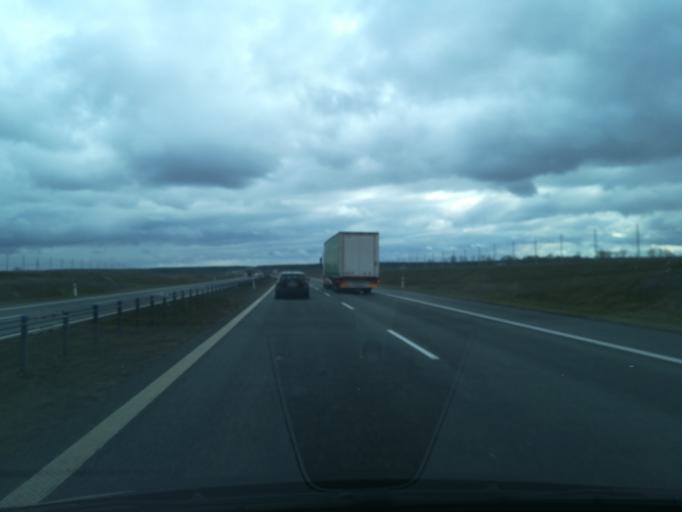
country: PL
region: Kujawsko-Pomorskie
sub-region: Powiat wabrzeski
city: Pluznica
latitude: 53.1796
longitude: 18.7376
